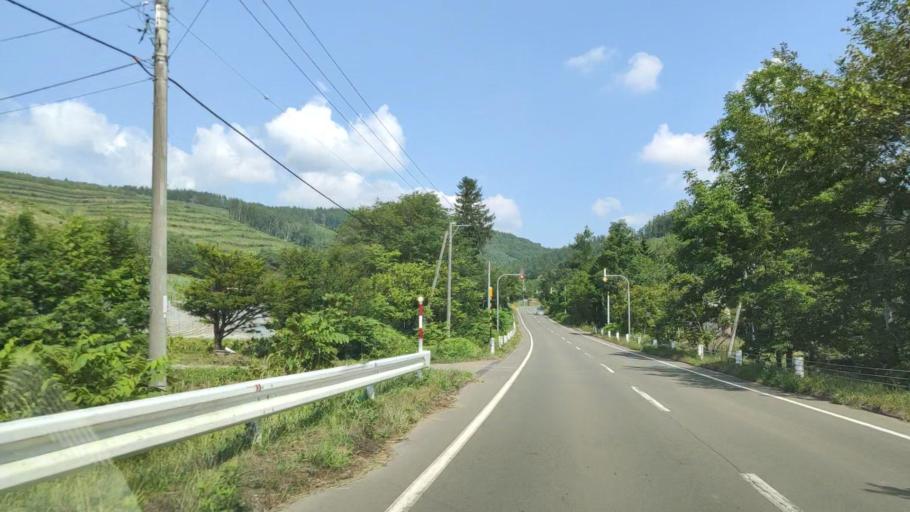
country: JP
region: Hokkaido
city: Shimo-furano
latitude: 43.4227
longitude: 142.4009
